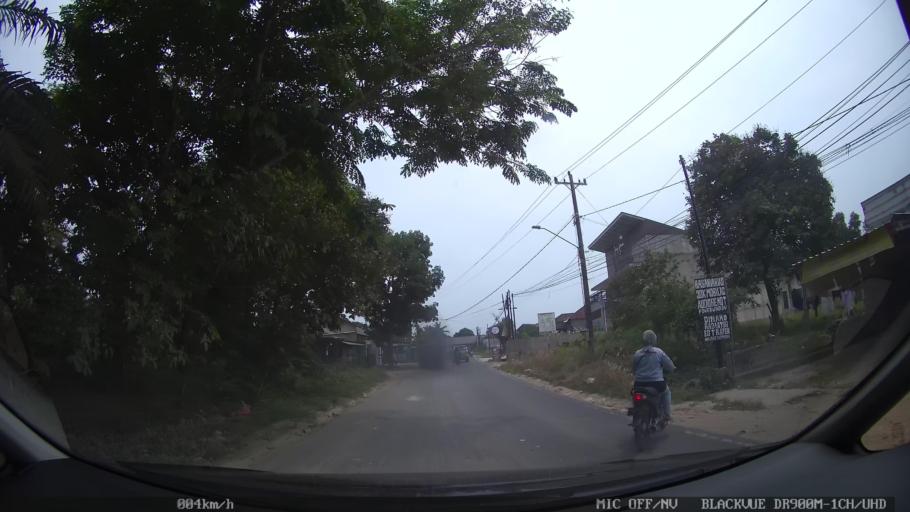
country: ID
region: Lampung
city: Kedaton
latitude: -5.4055
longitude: 105.3182
